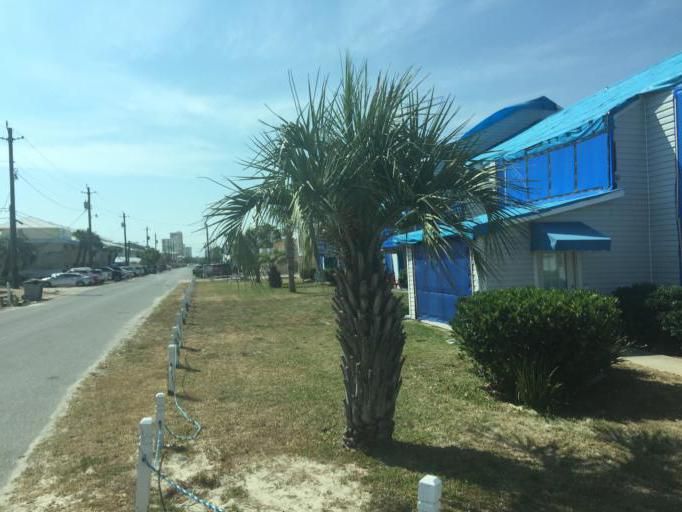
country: US
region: Florida
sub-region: Bay County
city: Panama City Beach
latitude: 30.1607
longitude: -85.7805
